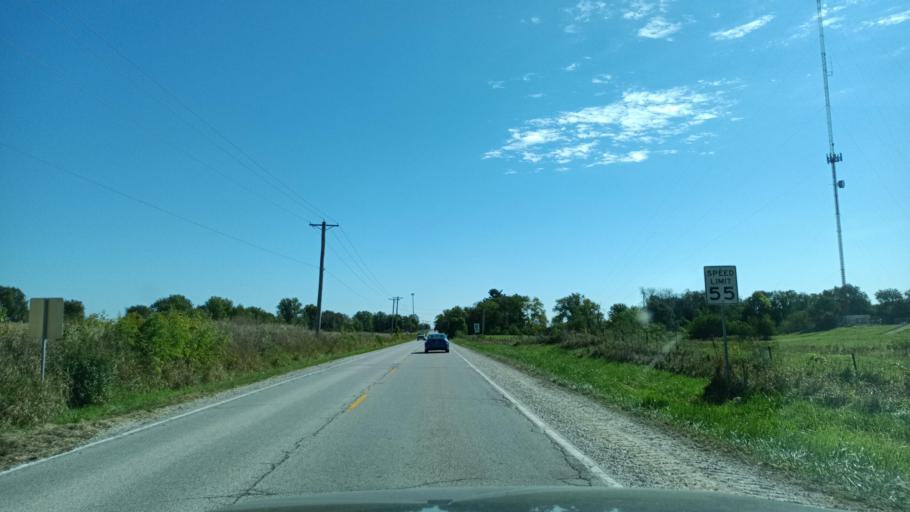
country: US
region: Illinois
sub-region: Knox County
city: Knoxville
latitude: 40.9080
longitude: -90.2685
